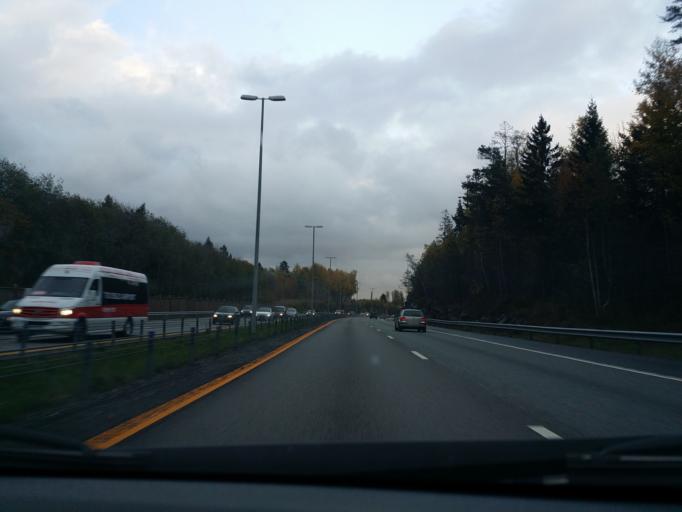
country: NO
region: Akershus
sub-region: Asker
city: Asker
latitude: 59.8260
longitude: 10.3867
